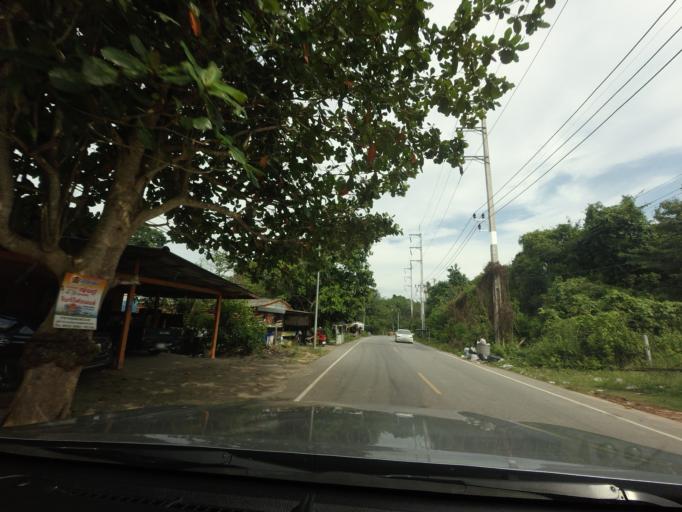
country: TH
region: Yala
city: Yala
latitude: 6.5077
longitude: 101.2888
